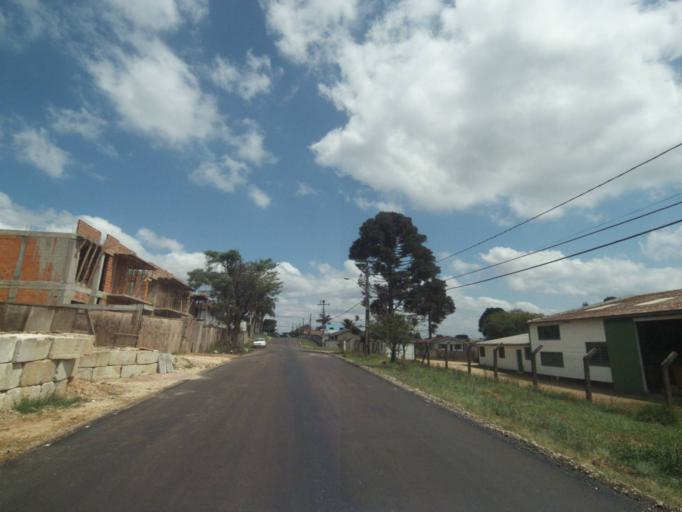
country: BR
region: Parana
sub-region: Curitiba
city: Curitiba
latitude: -25.5097
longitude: -49.3063
